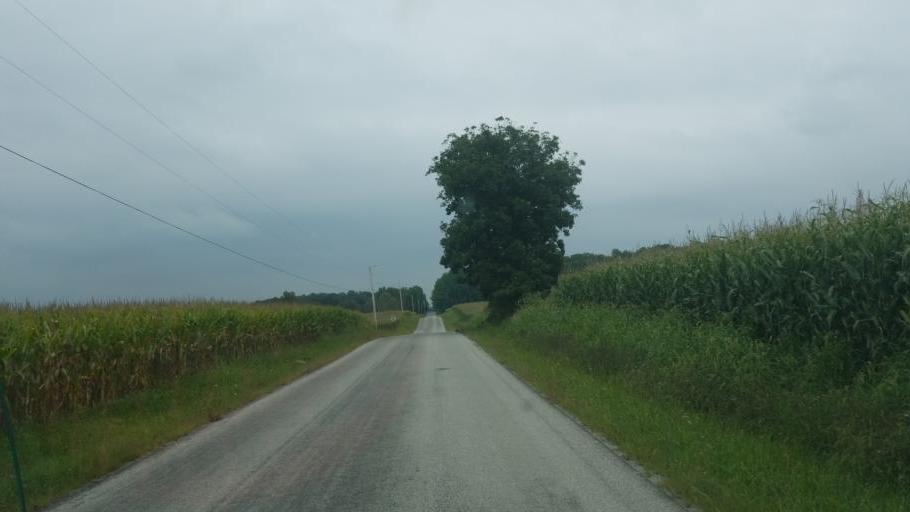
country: US
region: Ohio
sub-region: Medina County
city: Lodi
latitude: 40.9599
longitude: -81.9943
